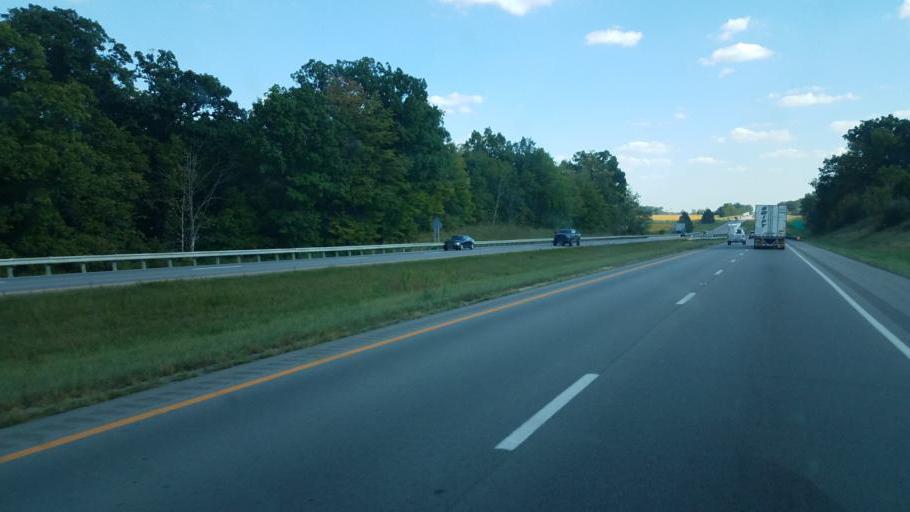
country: US
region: Ohio
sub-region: Wyandot County
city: Upper Sandusky
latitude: 40.8514
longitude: -83.2623
